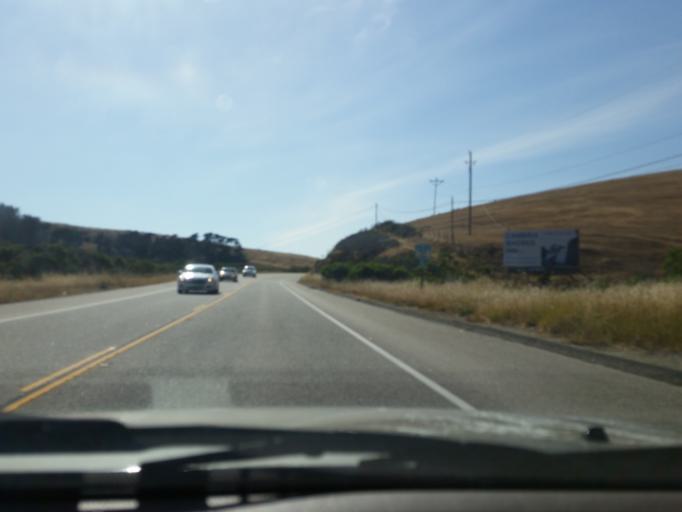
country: US
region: California
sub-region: San Luis Obispo County
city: Cayucos
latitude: 35.4732
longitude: -120.9850
